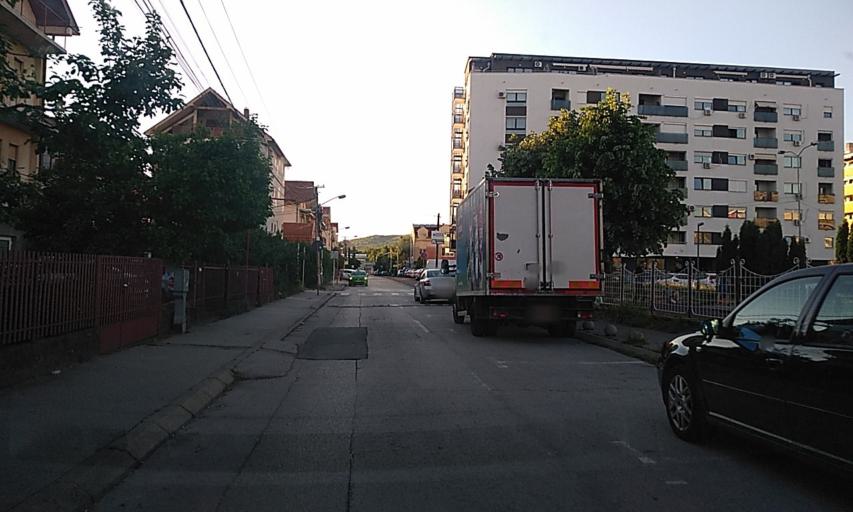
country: RS
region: Central Serbia
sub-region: Nisavski Okrug
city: Nis
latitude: 43.3208
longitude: 21.9301
